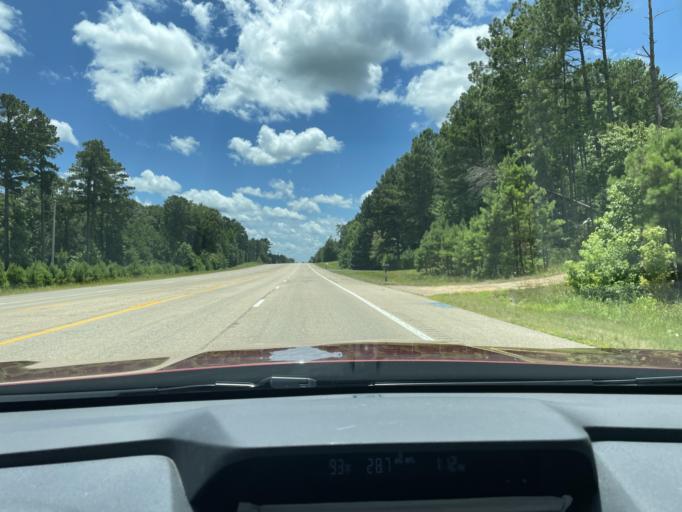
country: US
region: Arkansas
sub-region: Drew County
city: Monticello
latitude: 33.6900
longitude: -91.8061
